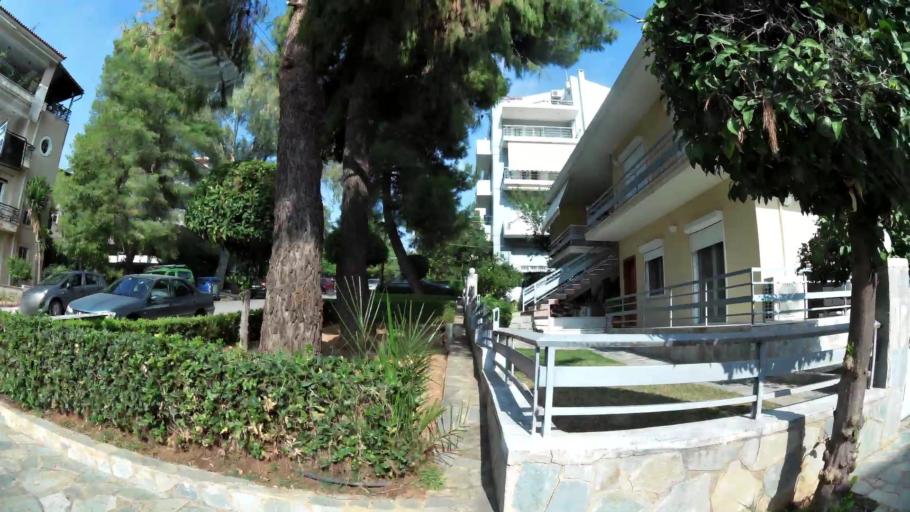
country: GR
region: Attica
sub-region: Nomos Attikis
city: Zografos
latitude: 37.9790
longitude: 23.7912
